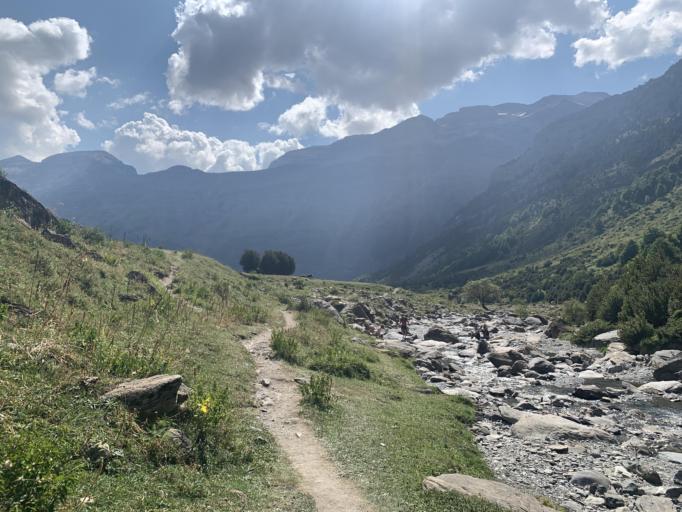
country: ES
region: Aragon
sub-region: Provincia de Huesca
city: Bielsa
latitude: 42.6968
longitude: 0.0916
